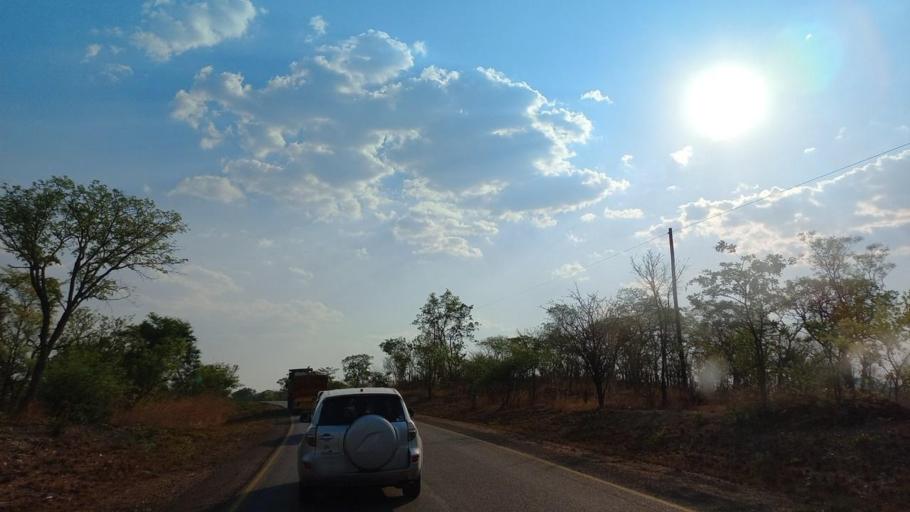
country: ZM
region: Lusaka
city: Luangwa
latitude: -14.9797
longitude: 29.9915
